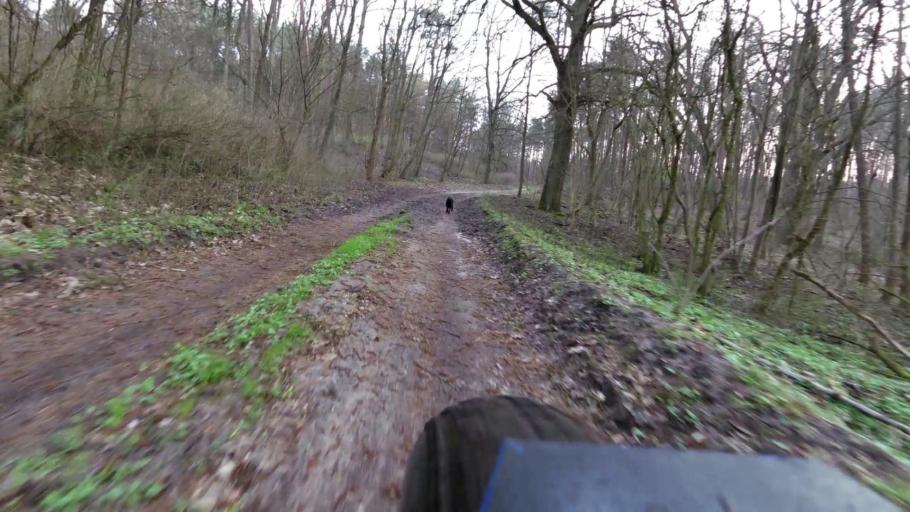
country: DE
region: Brandenburg
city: Vogelsang
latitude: 52.2793
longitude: 14.6966
